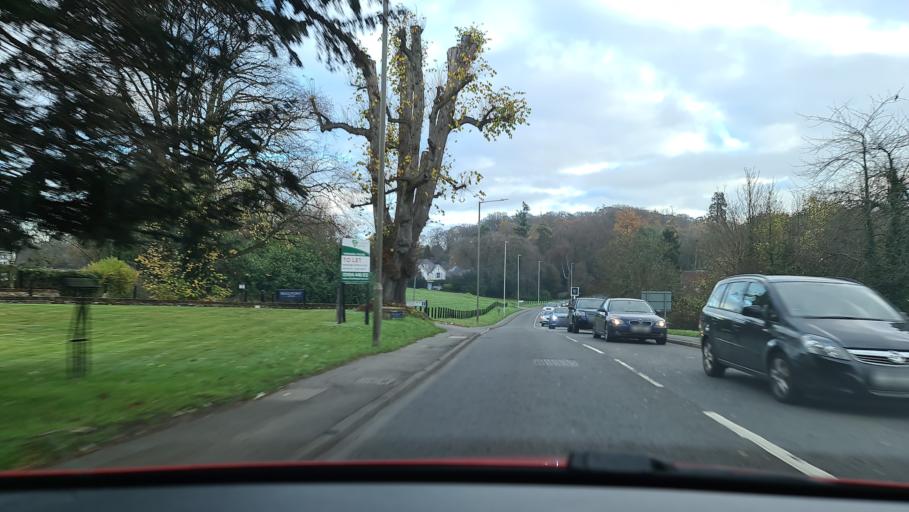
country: GB
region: England
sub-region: Buckinghamshire
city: High Wycombe
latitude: 51.6456
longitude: -0.7295
